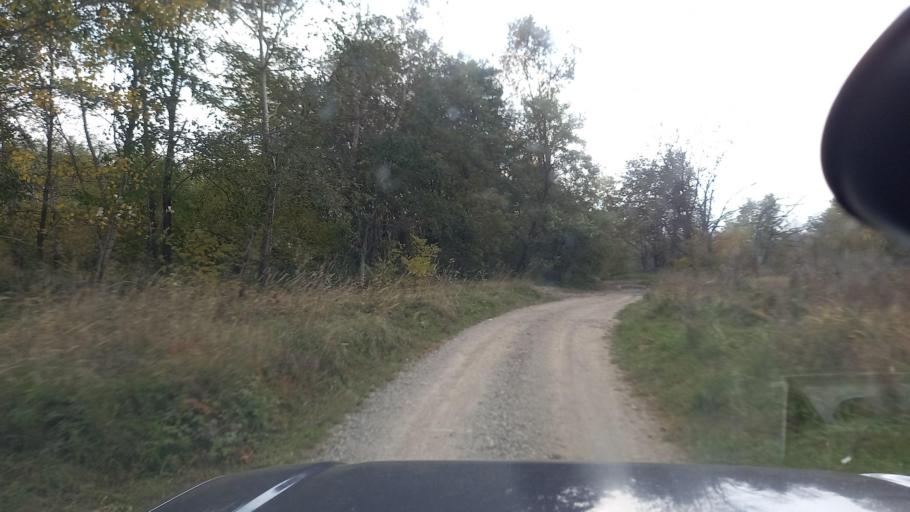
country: RU
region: Krasnodarskiy
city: Shedok
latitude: 44.1772
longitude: 40.8508
